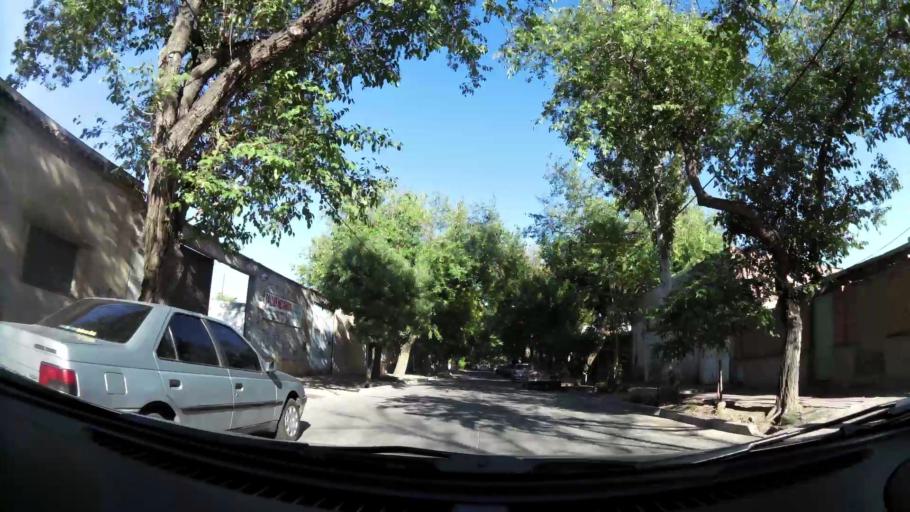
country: AR
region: Mendoza
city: Mendoza
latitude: -32.8743
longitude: -68.8266
